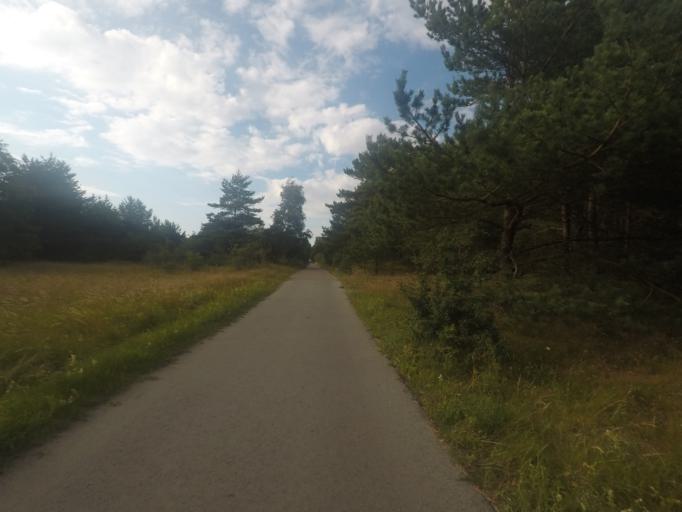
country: LT
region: Klaipedos apskritis
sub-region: Klaipeda
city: Klaipeda
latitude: 55.6846
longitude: 21.1040
